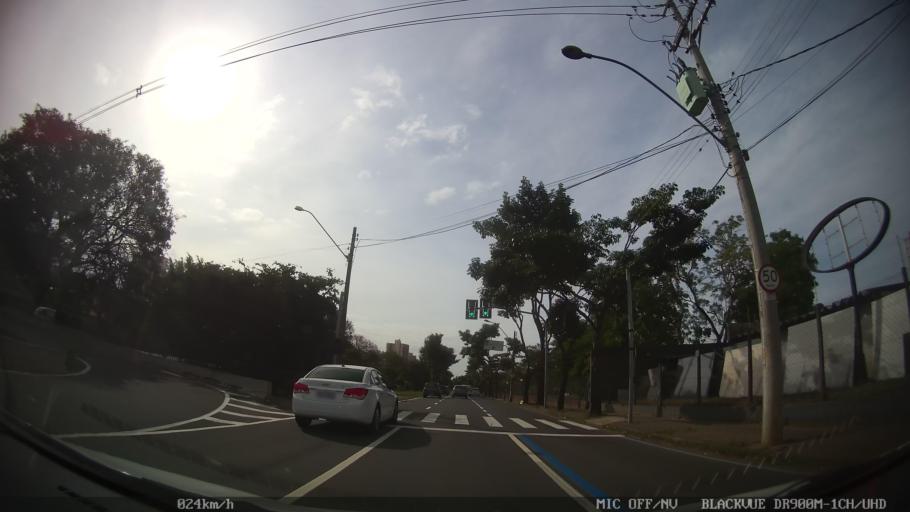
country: BR
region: Sao Paulo
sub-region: Piracicaba
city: Piracicaba
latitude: -22.7342
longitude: -47.6286
